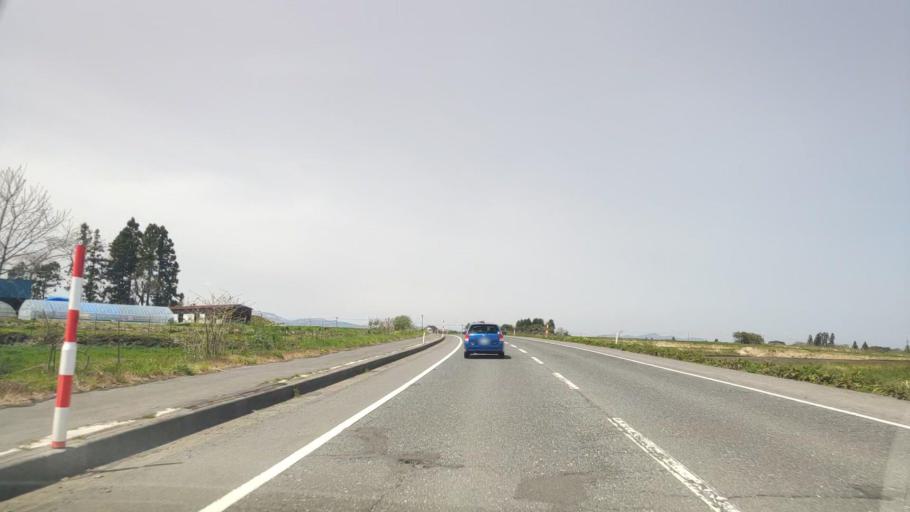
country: JP
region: Aomori
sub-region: Misawa Shi
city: Inuotose
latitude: 40.6368
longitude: 141.2420
